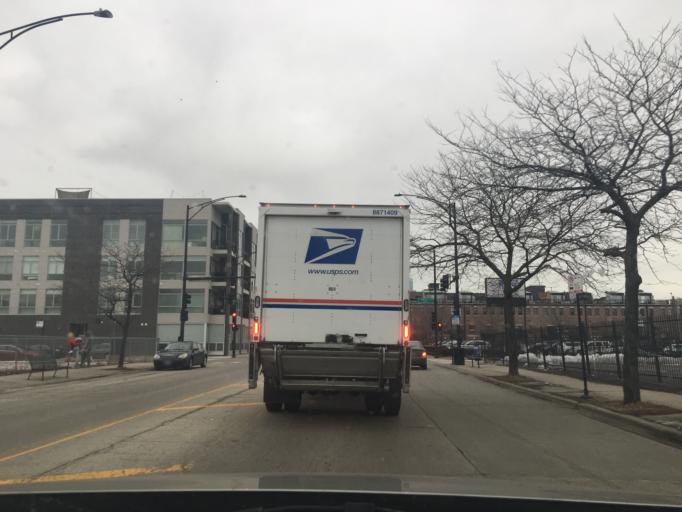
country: US
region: Illinois
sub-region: Cook County
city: Chicago
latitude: 41.8812
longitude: -87.6846
